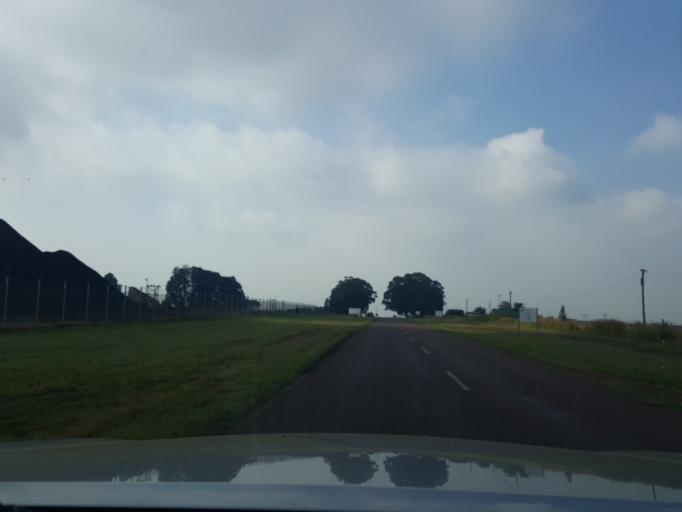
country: ZA
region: Mpumalanga
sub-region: Nkangala District Municipality
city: Middelburg
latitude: -25.9760
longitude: 29.4509
